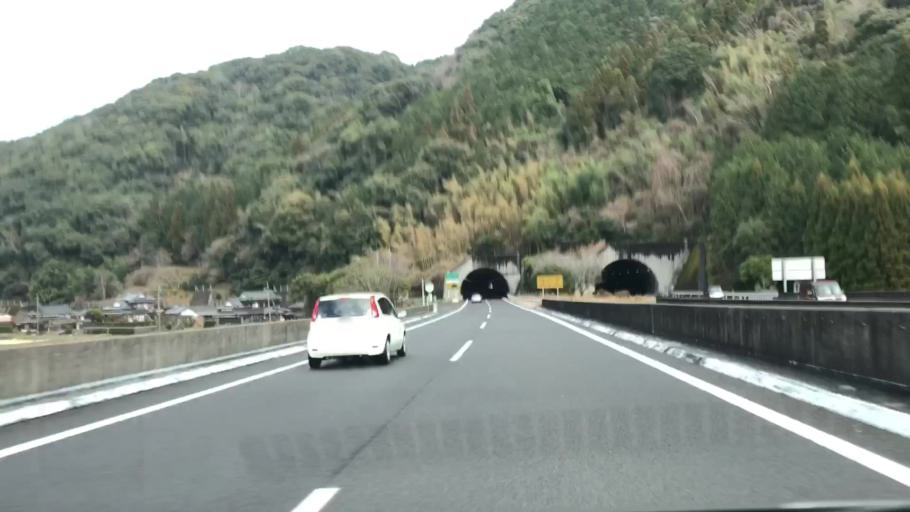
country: JP
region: Saga Prefecture
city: Takeocho-takeo
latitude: 33.1719
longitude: 130.0404
